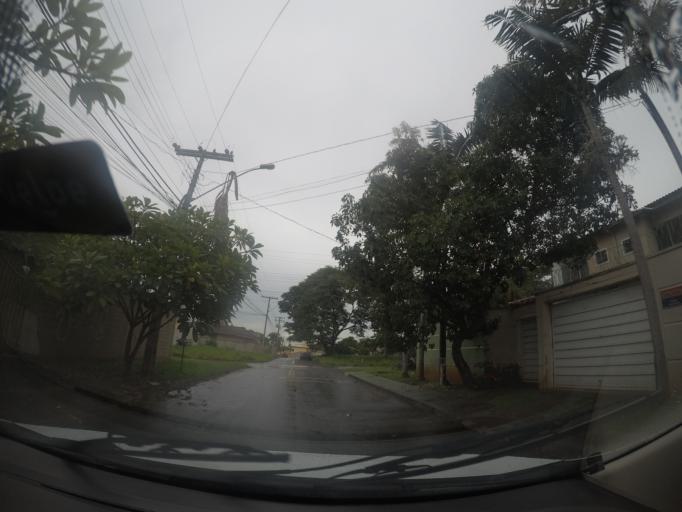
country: BR
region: Goias
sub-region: Goiania
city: Goiania
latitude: -16.6443
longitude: -49.2297
